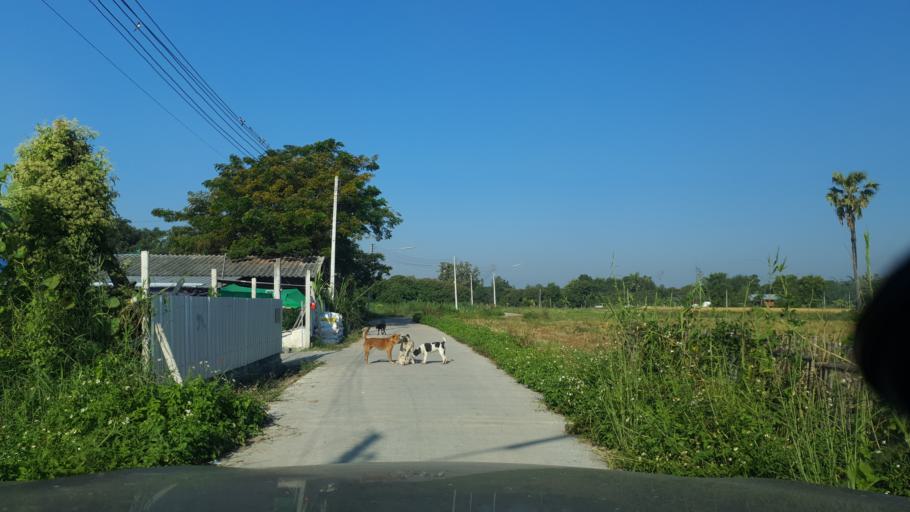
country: TH
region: Chiang Mai
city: San Kamphaeng
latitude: 18.6895
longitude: 99.1482
